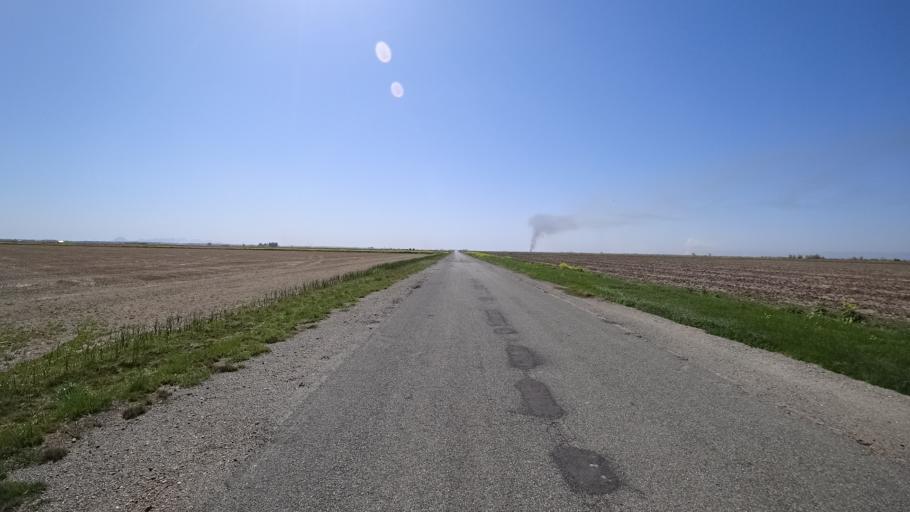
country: US
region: California
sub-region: Glenn County
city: Willows
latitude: 39.4424
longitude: -122.0645
